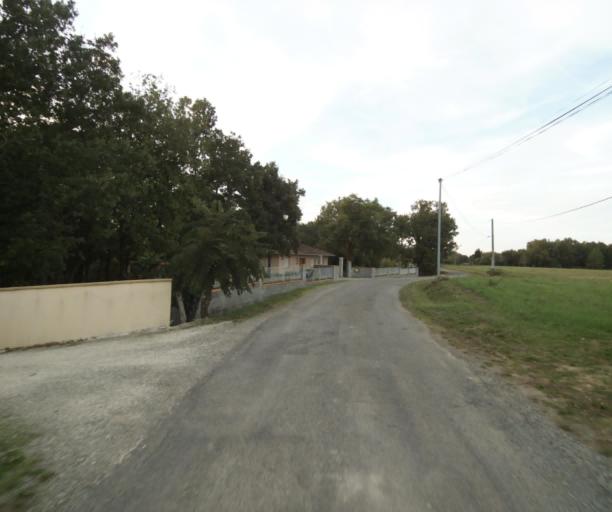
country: FR
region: Midi-Pyrenees
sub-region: Departement du Tarn-et-Garonne
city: Pompignan
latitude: 43.8230
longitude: 1.3152
